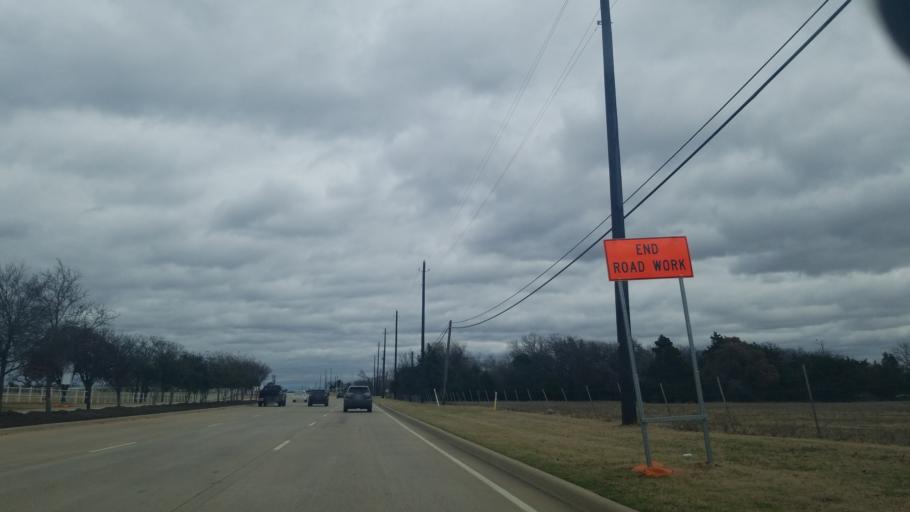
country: US
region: Texas
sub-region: Denton County
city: Double Oak
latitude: 33.0461
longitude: -97.1256
